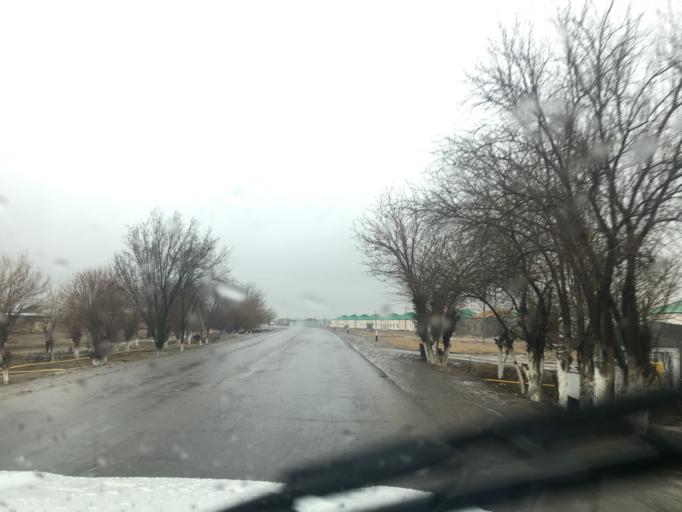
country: TM
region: Mary
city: Yoloeten
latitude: 37.2948
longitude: 62.3338
